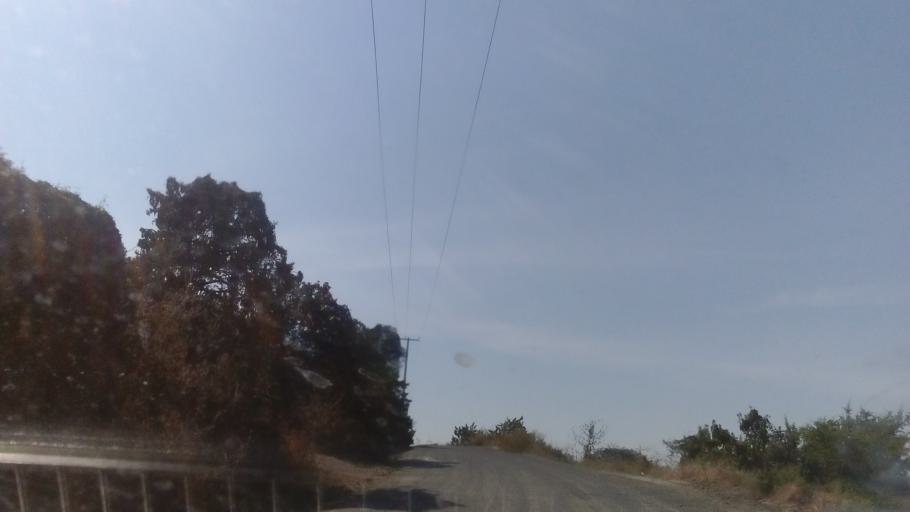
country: MX
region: Guanajuato
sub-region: Leon
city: Medina
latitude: 21.1459
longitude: -101.6060
